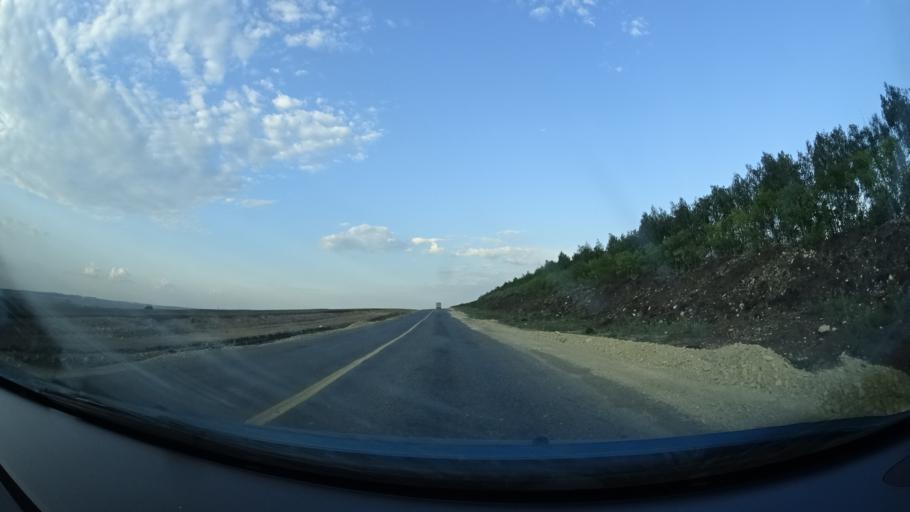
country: RU
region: Samara
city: Kamyshla
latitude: 54.0350
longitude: 51.9408
